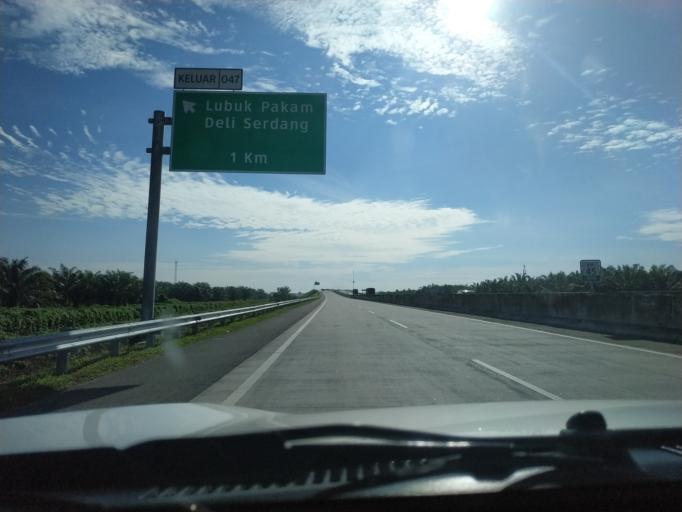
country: ID
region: North Sumatra
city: Perbaungan
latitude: 3.5315
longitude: 98.8817
